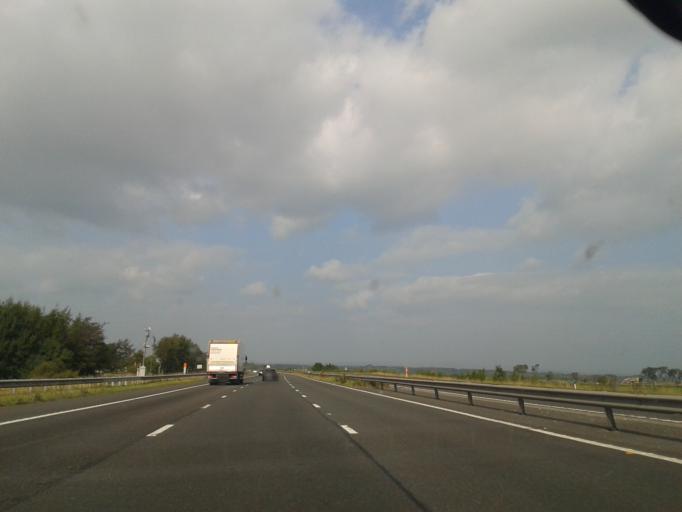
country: GB
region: Scotland
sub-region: Dumfries and Galloway
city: Gretna
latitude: 54.9702
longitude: -3.0034
